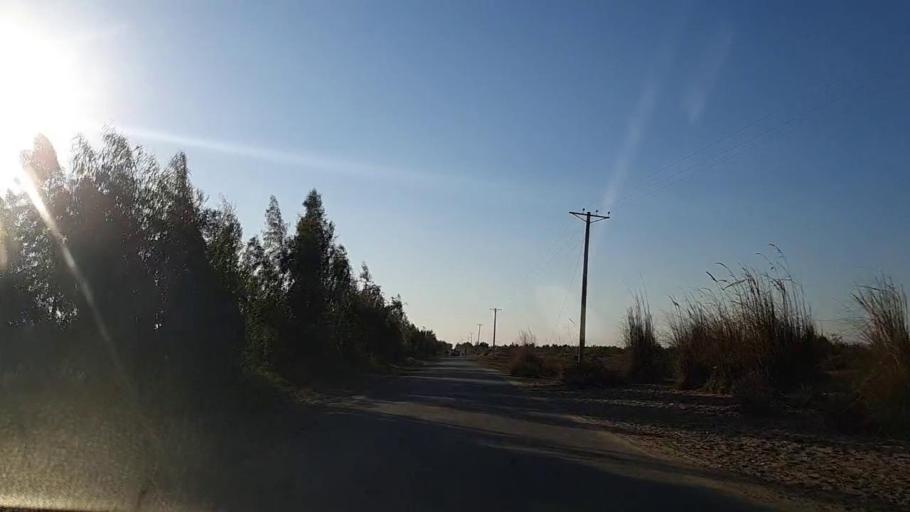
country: PK
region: Sindh
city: Khadro
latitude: 26.2790
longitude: 68.9084
